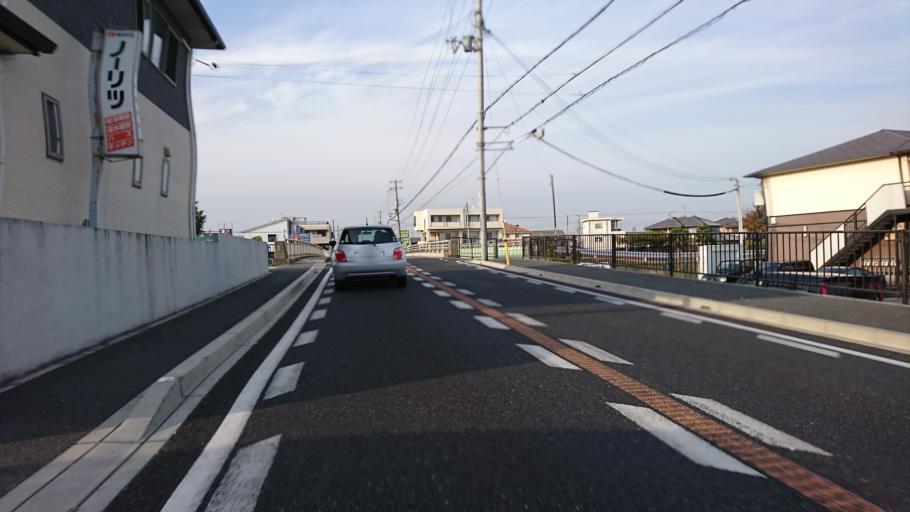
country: JP
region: Hyogo
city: Kakogawacho-honmachi
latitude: 34.7143
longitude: 134.8618
